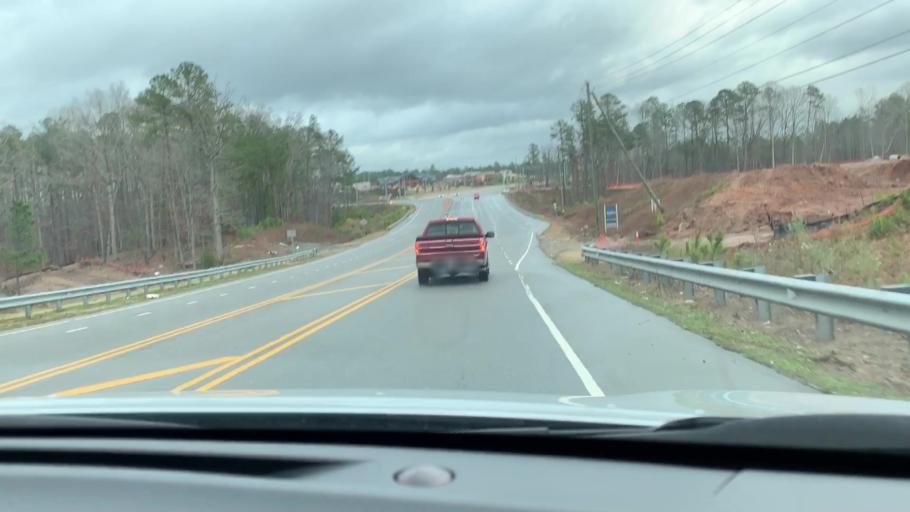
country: US
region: North Carolina
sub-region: Wake County
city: Green Level
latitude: 35.8444
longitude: -78.8940
